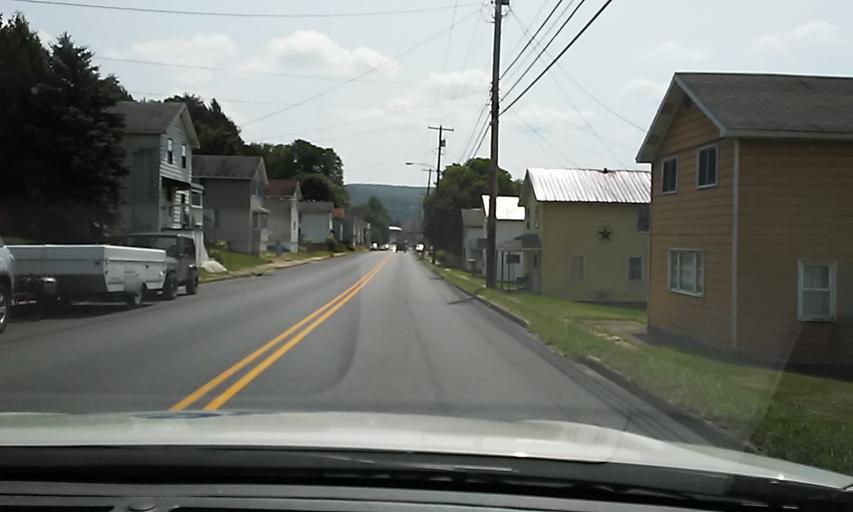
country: US
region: Pennsylvania
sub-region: Elk County
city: Ridgway
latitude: 41.4302
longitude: -78.7340
